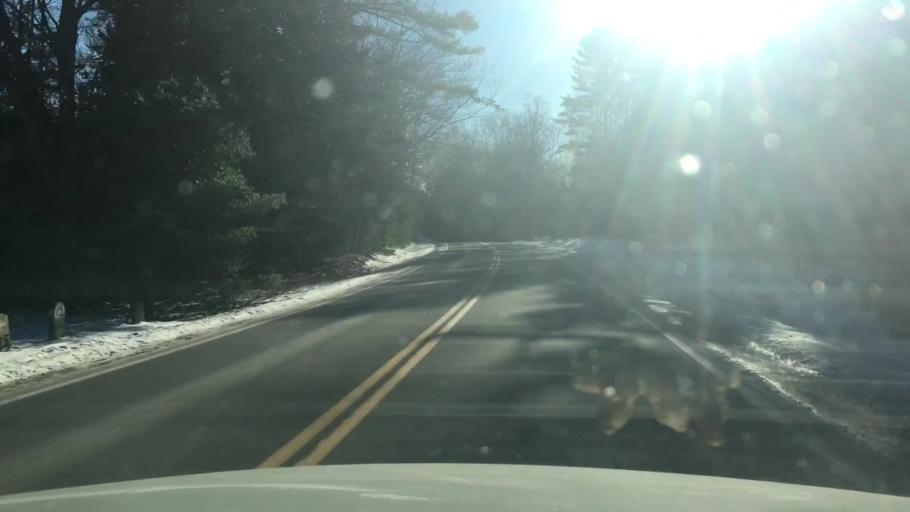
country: US
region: Maine
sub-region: Hancock County
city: Orland
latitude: 44.5143
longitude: -68.7525
